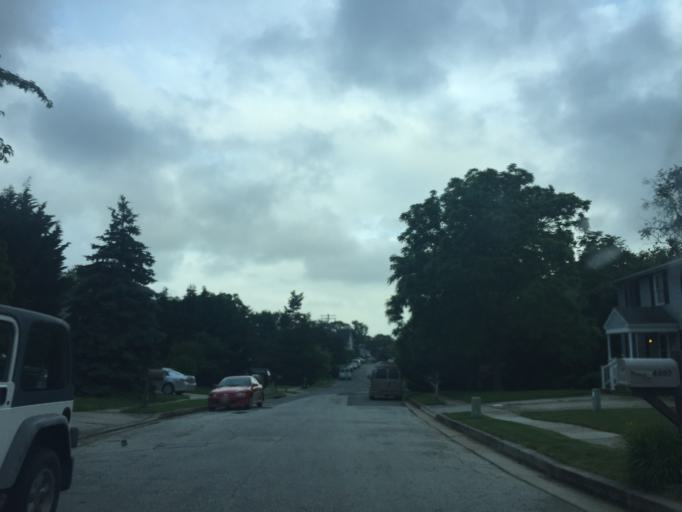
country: US
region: Maryland
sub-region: Baltimore County
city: Carney
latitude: 39.3926
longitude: -76.4940
